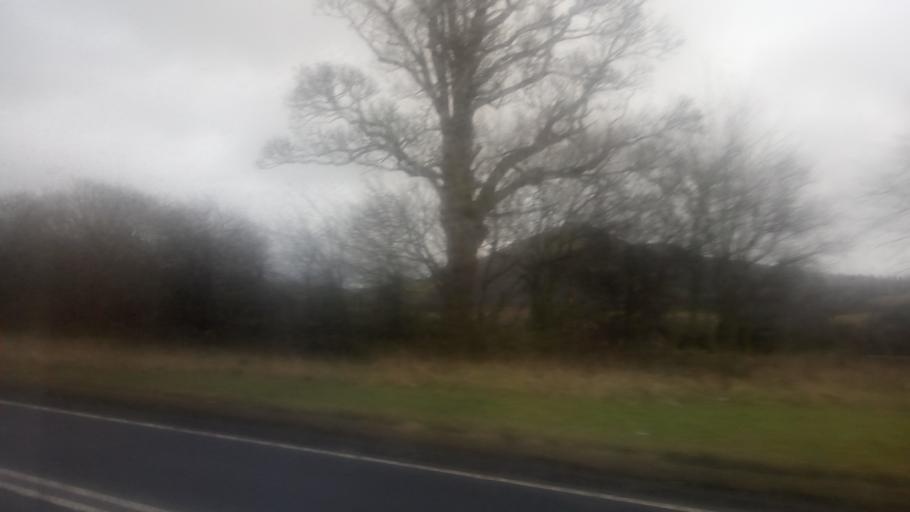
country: GB
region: Scotland
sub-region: The Scottish Borders
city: Earlston
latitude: 55.6148
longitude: -2.6783
